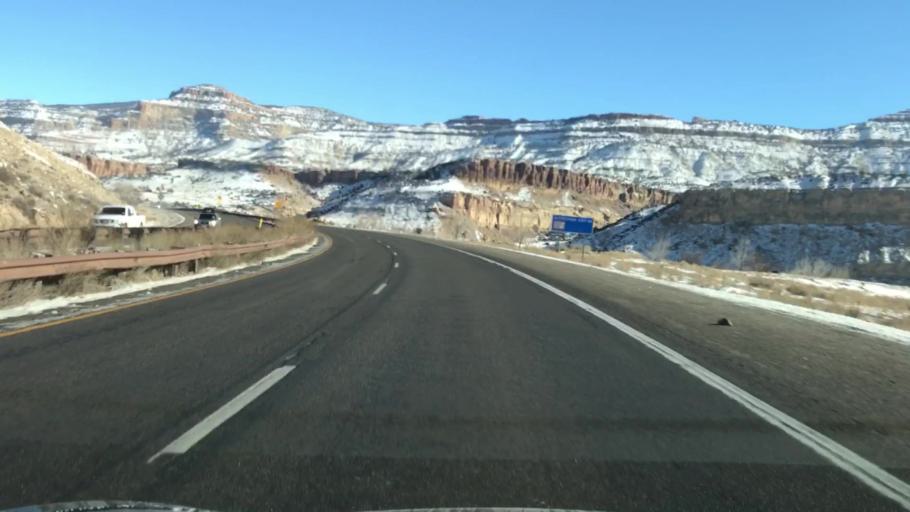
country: US
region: Colorado
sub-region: Mesa County
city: Palisade
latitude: 39.1177
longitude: -108.3297
